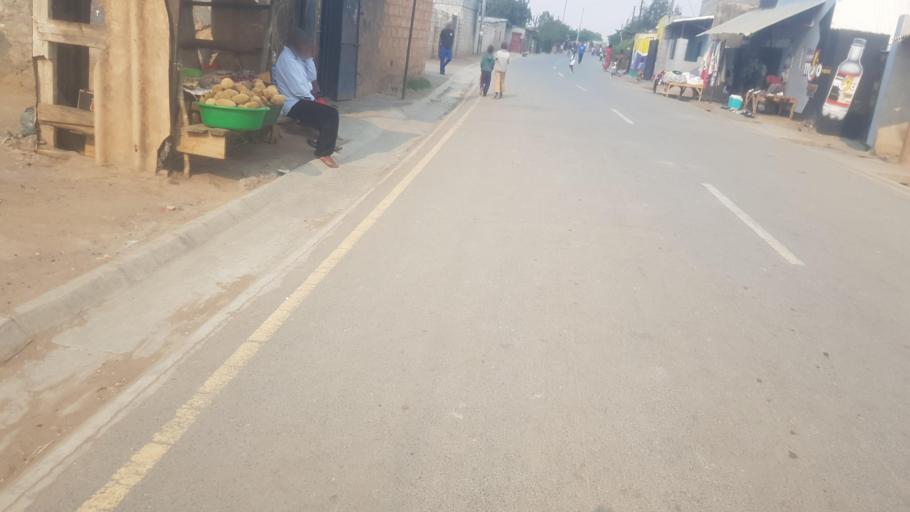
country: ZM
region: Lusaka
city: Lusaka
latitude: -15.4409
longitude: 28.3794
